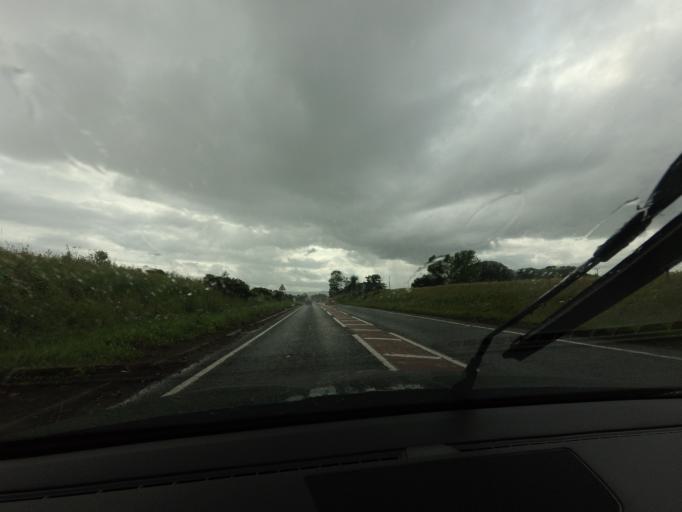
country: GB
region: Scotland
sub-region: Highland
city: Fortrose
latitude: 57.5147
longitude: -4.0893
